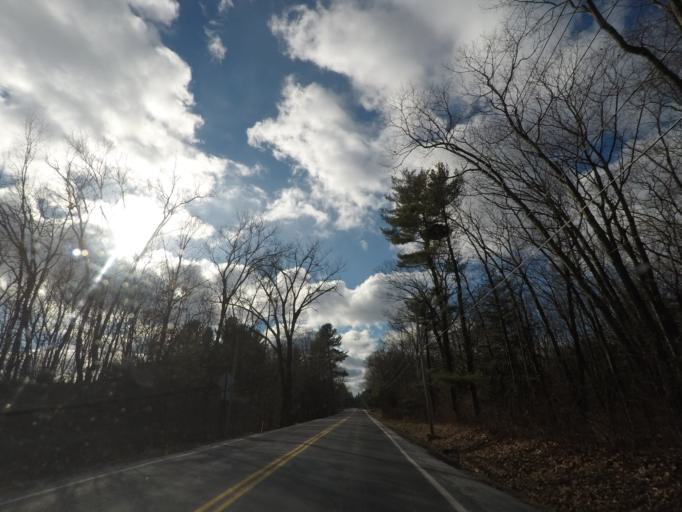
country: US
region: New York
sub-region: Schenectady County
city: East Glenville
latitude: 42.8845
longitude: -73.8823
